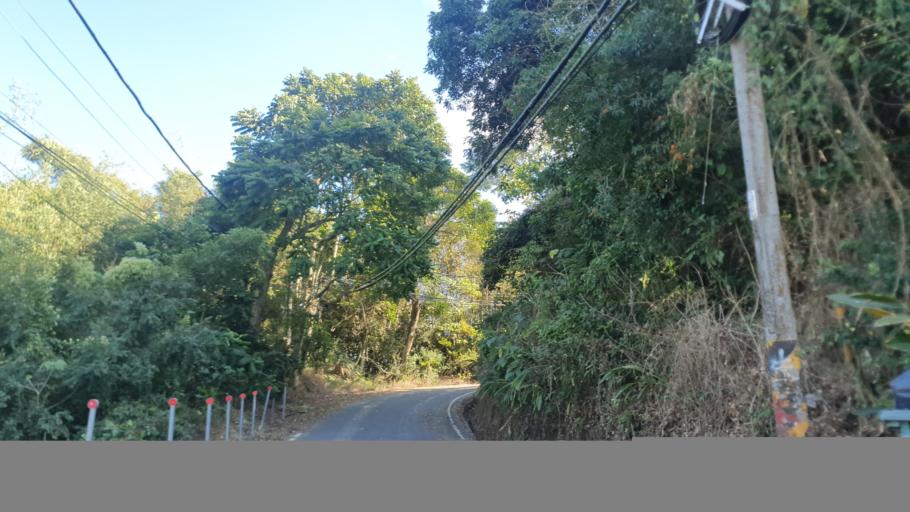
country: TW
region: Taiwan
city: Yujing
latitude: 23.0315
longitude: 120.3852
